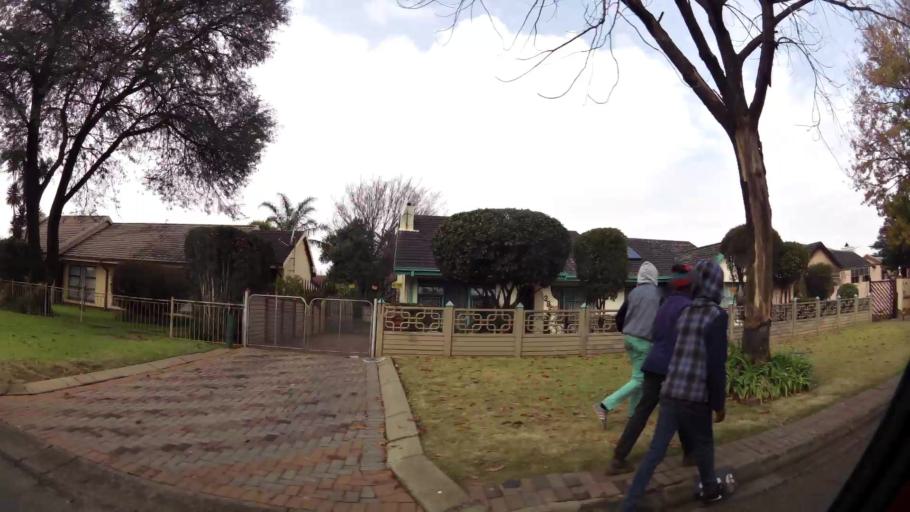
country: ZA
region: Gauteng
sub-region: Sedibeng District Municipality
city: Vanderbijlpark
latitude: -26.6962
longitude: 27.8502
